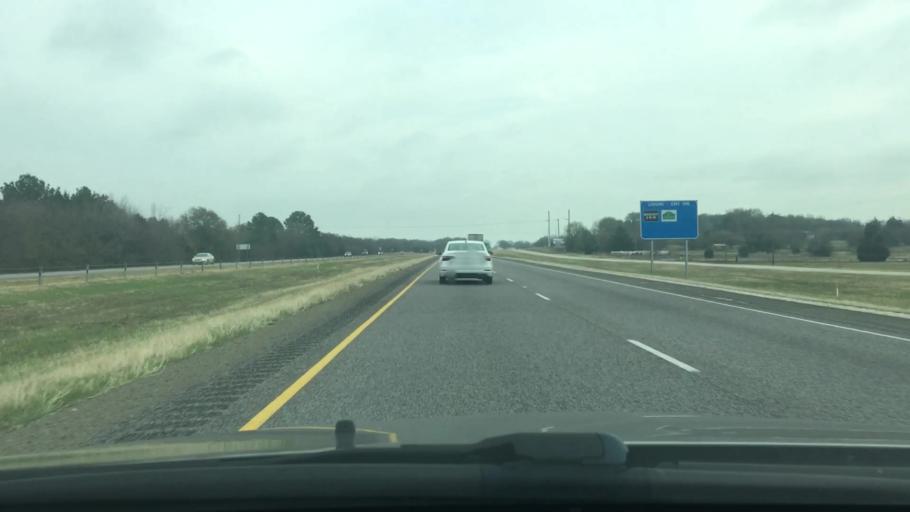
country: US
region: Texas
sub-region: Freestone County
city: Fairfield
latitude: 31.7383
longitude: -96.1884
